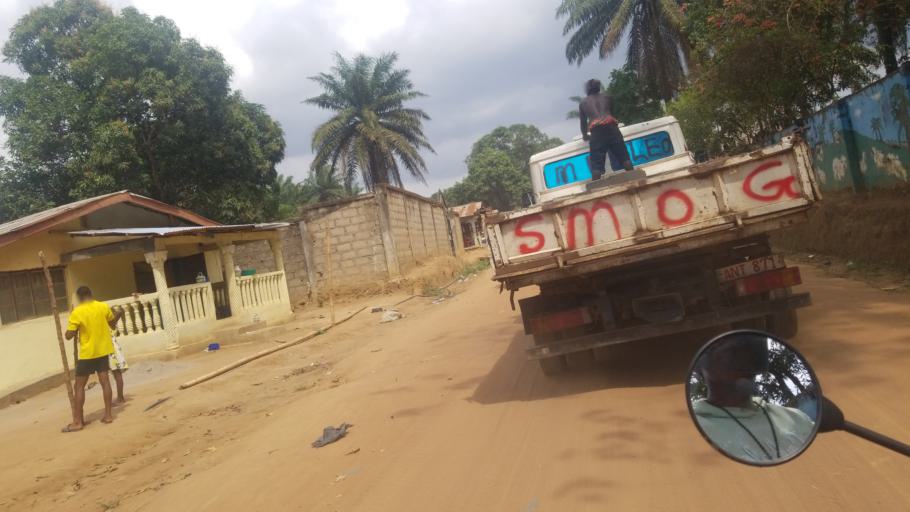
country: SL
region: Western Area
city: Waterloo
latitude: 8.3316
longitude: -13.0410
